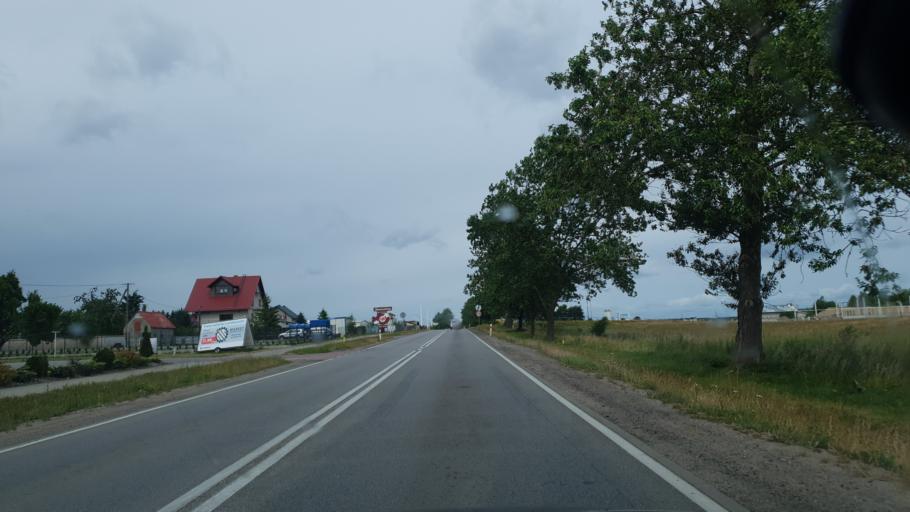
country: PL
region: Pomeranian Voivodeship
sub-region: Powiat kartuski
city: Banino
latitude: 54.4181
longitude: 18.3775
